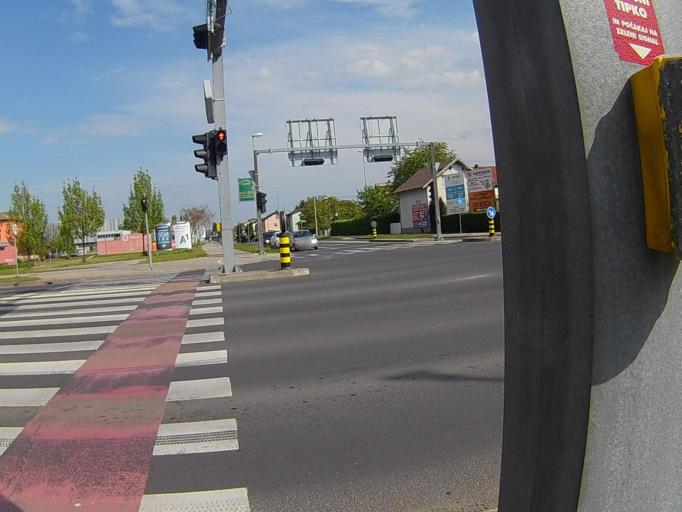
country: SI
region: Maribor
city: Kamnica
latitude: 46.5531
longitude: 15.6234
